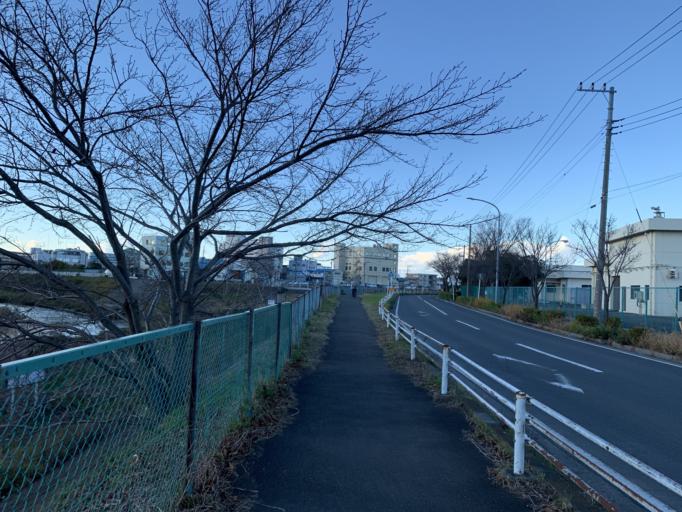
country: JP
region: Tokyo
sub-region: Machida-shi
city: Machida
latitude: 35.5141
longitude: 139.5520
